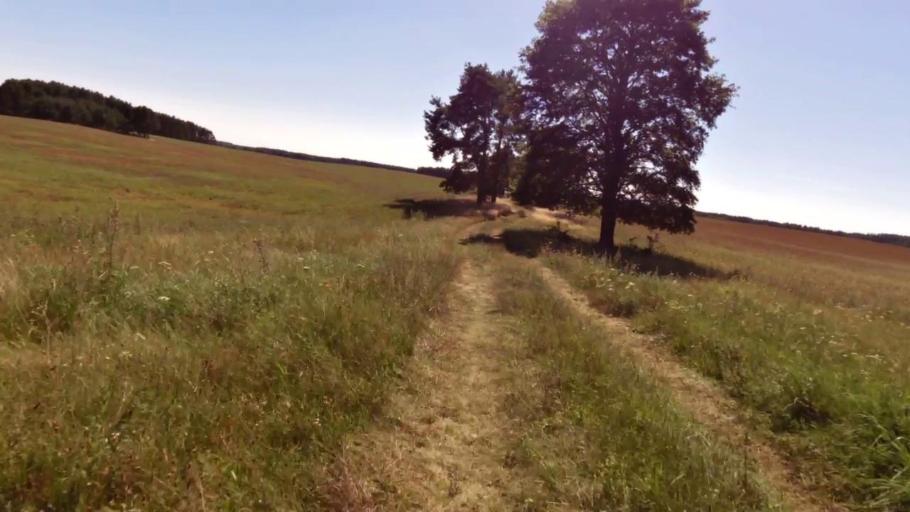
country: PL
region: West Pomeranian Voivodeship
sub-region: Powiat szczecinecki
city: Bialy Bor
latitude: 53.8480
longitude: 16.7520
